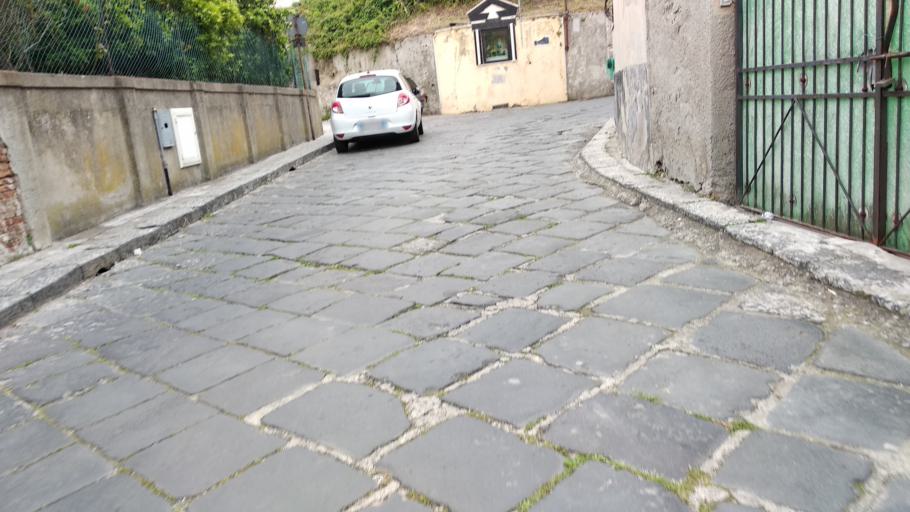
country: IT
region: Sicily
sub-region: Messina
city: Saponara Marittima
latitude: 38.2344
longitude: 15.4301
